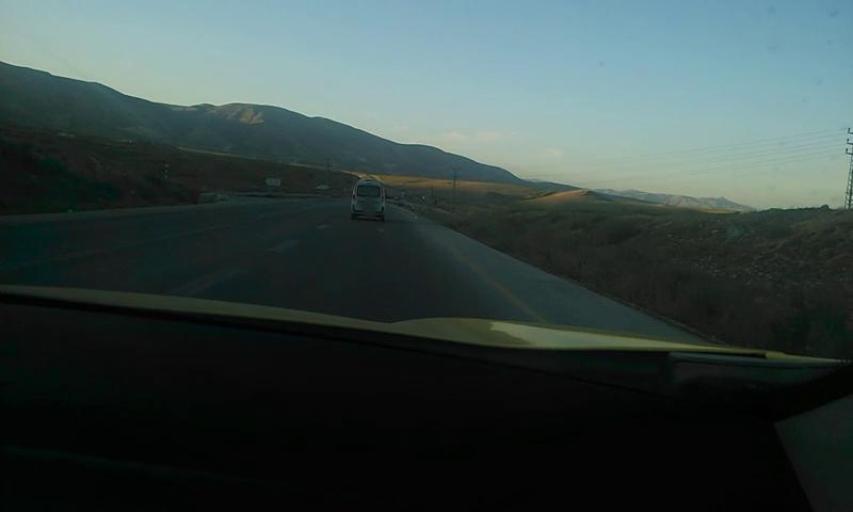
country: PS
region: West Bank
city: An Nuway`imah
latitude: 31.9151
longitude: 35.4209
